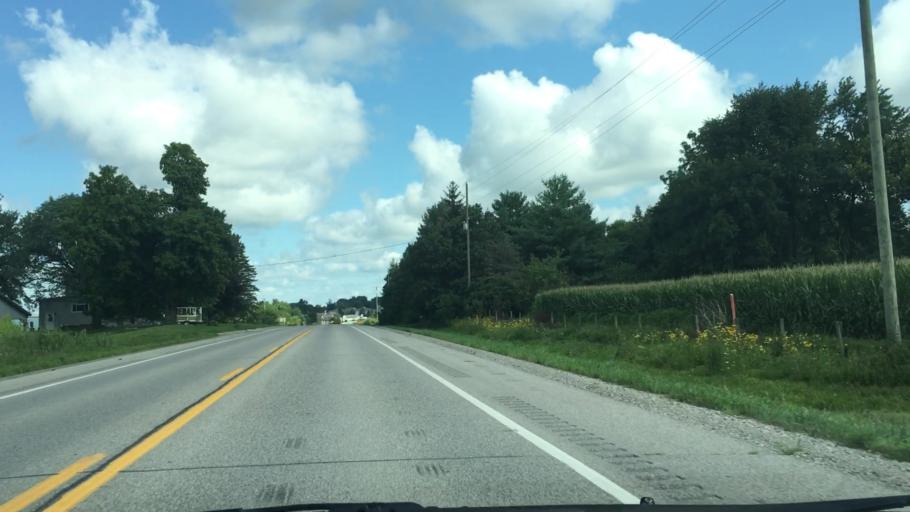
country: US
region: Iowa
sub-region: Johnson County
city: Solon
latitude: 41.7905
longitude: -91.4883
